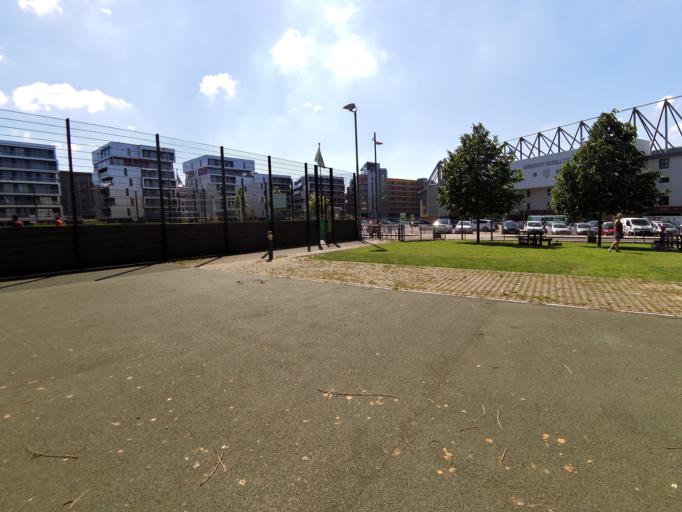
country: GB
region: England
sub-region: Norfolk
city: Thorpe Hamlet
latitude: 52.6215
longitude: 1.3116
